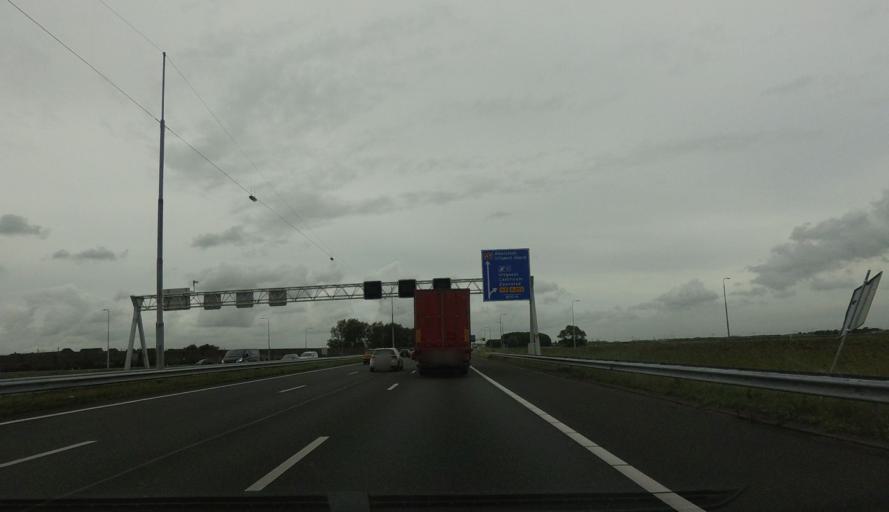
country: NL
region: North Holland
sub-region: Gemeente Uitgeest
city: Uitgeest
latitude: 52.5086
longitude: 4.7073
